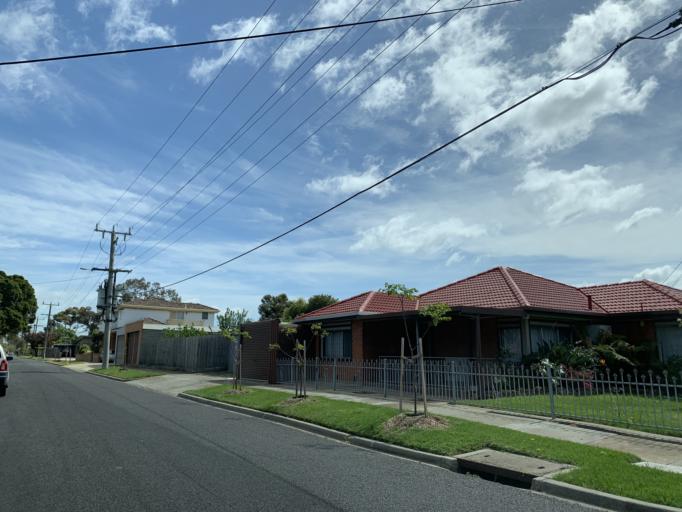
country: AU
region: Victoria
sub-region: Brimbank
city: Kealba
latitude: -37.7451
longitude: 144.8195
